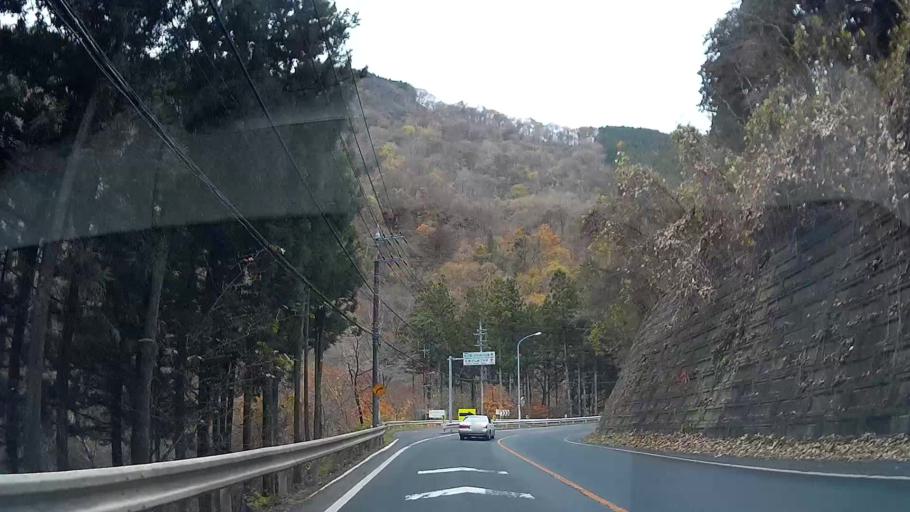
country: JP
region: Saitama
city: Chichibu
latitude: 35.9371
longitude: 138.9613
